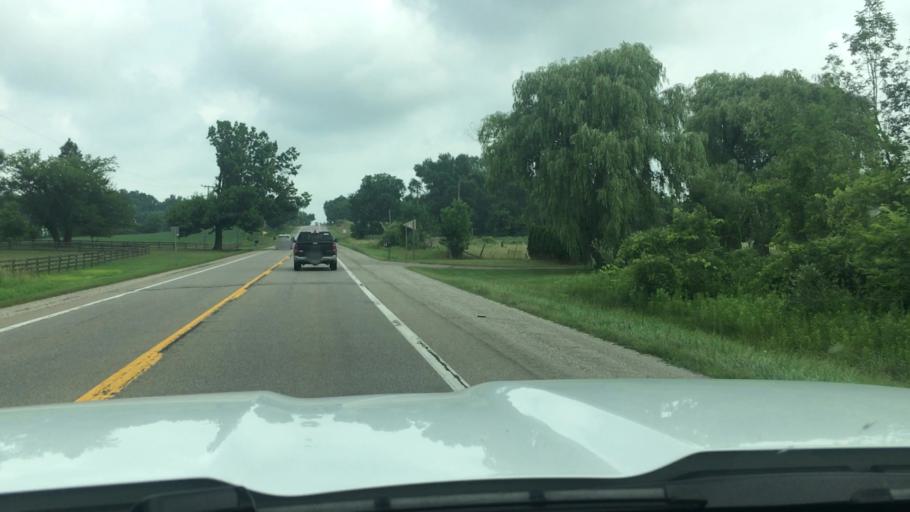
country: US
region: Michigan
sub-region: Lapeer County
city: Imlay City
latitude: 43.0689
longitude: -83.0748
